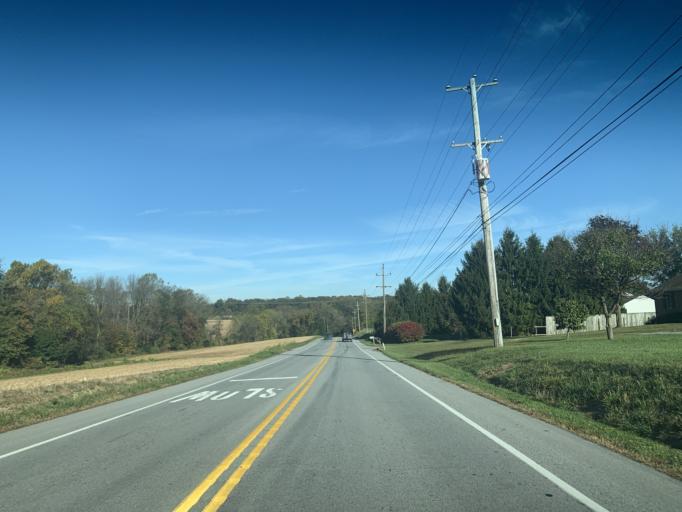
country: US
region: Pennsylvania
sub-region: Chester County
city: Parkesburg
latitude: 39.9415
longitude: -75.9128
